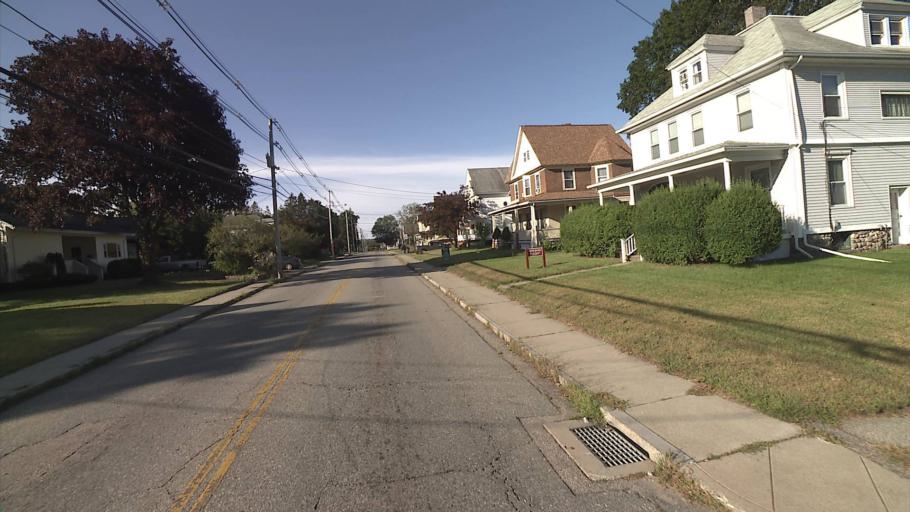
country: US
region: Connecticut
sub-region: New London County
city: Norwich
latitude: 41.5145
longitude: -72.0816
